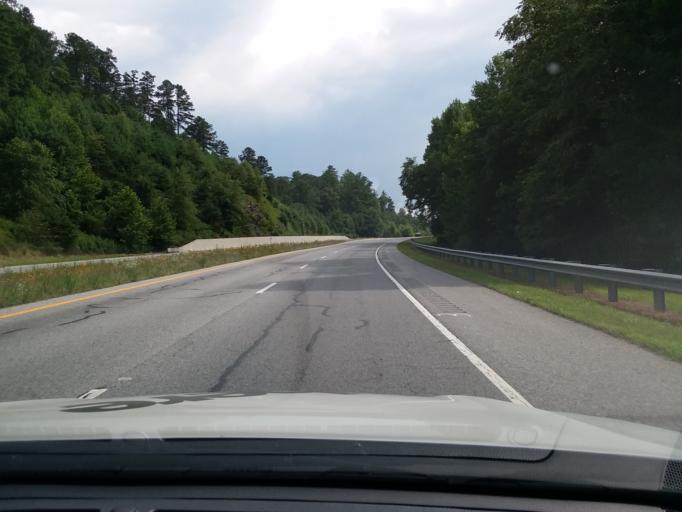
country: US
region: Georgia
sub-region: Rabun County
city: Clayton
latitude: 34.7729
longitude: -83.3950
